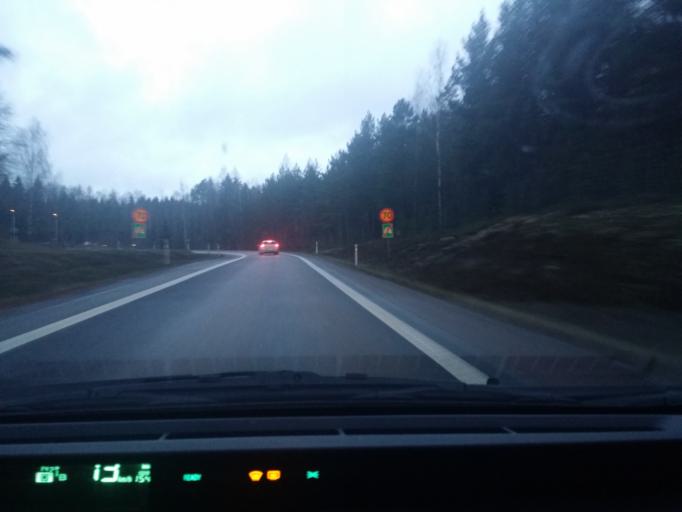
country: SE
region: Soedermanland
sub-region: Eskilstuna Kommun
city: Hallbybrunn
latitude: 59.4083
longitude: 16.3748
